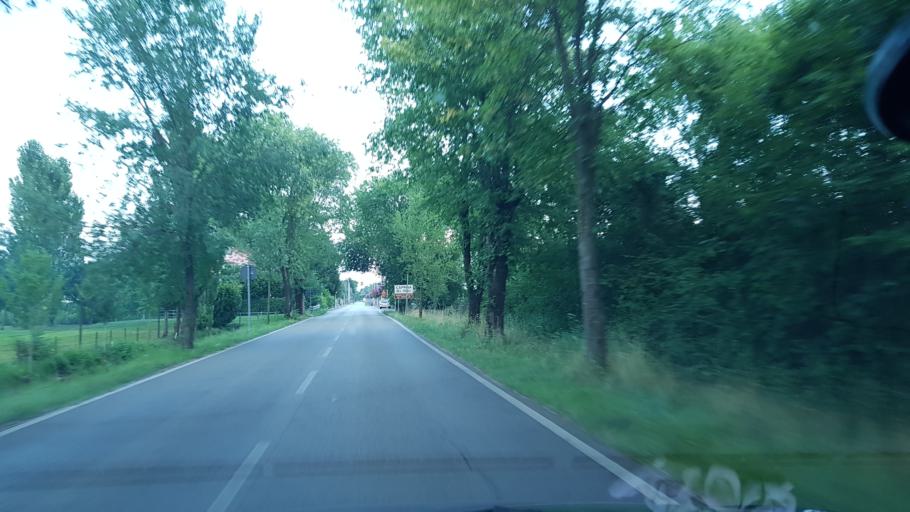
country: IT
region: Friuli Venezia Giulia
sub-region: Provincia di Gorizia
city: Capriva del Friuli
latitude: 45.9422
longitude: 13.5052
